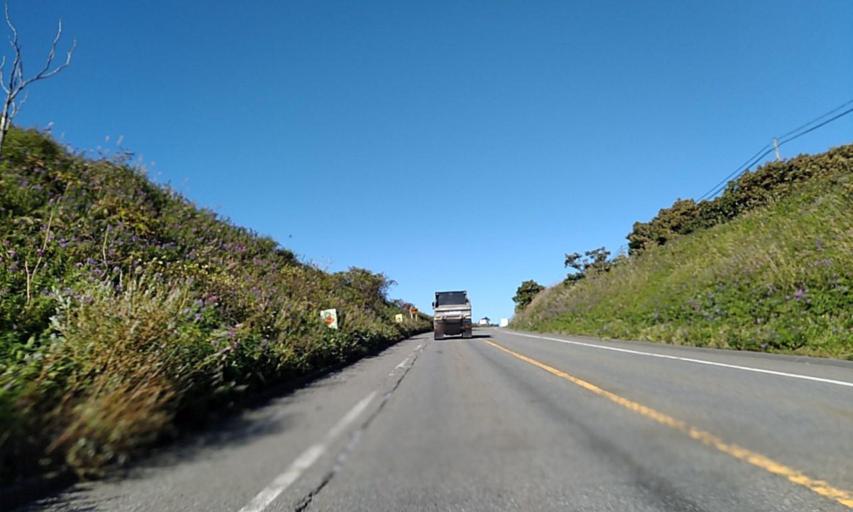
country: JP
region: Hokkaido
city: Shizunai-furukawacho
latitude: 42.4704
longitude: 142.1091
